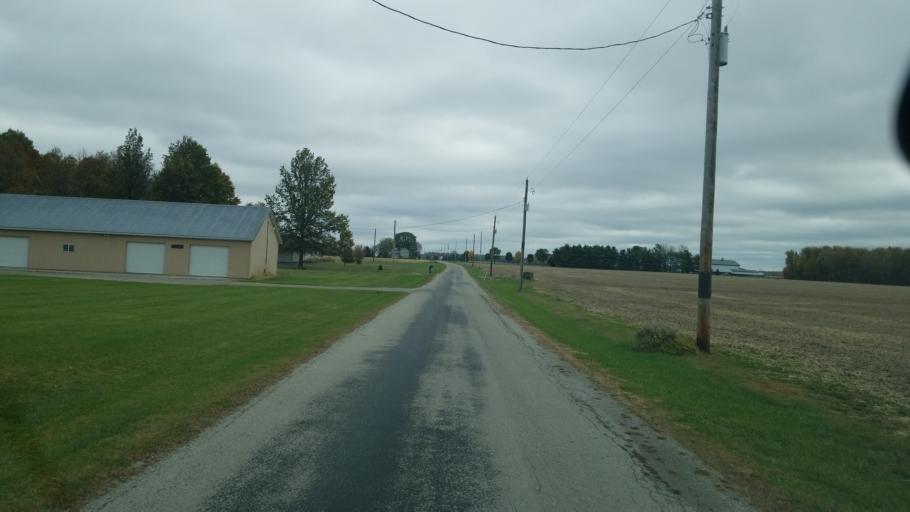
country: US
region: Ohio
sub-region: Huron County
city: Willard
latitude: 40.9315
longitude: -82.8386
